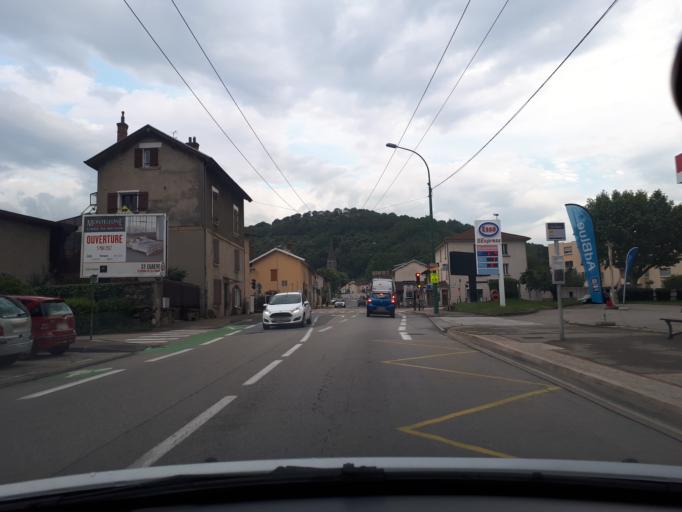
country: FR
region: Rhone-Alpes
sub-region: Departement de l'Isere
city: Eybens
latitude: 45.1505
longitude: 5.7499
